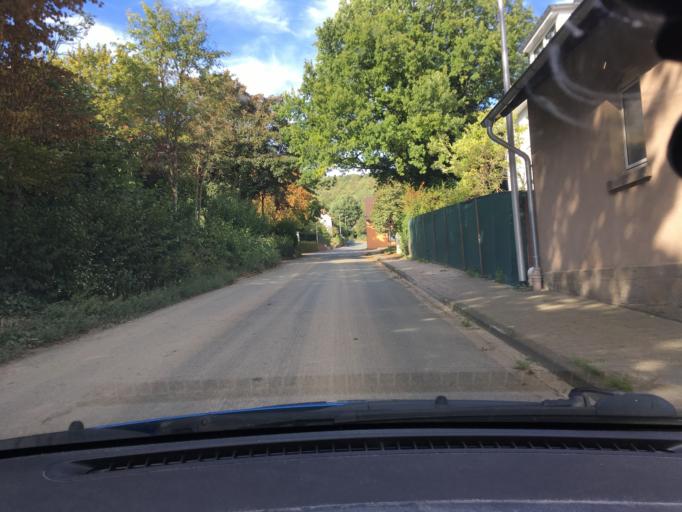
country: DE
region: Lower Saxony
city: Hameln
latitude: 52.1563
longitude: 9.3827
